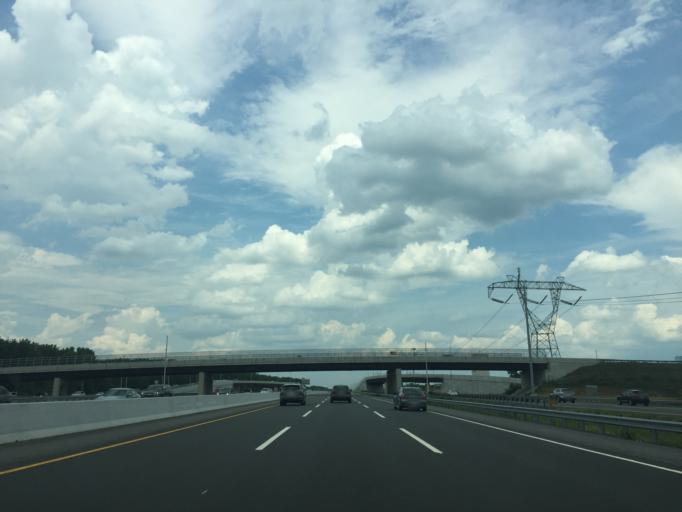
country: US
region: New Jersey
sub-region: Monmouth County
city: Allentown
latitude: 40.1953
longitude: -74.5983
